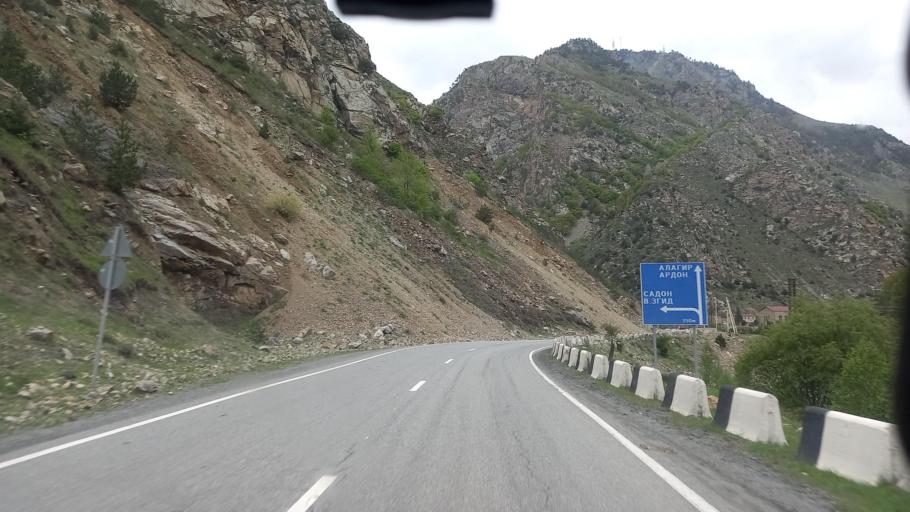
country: RU
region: North Ossetia
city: Mizur
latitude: 42.8357
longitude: 44.0270
